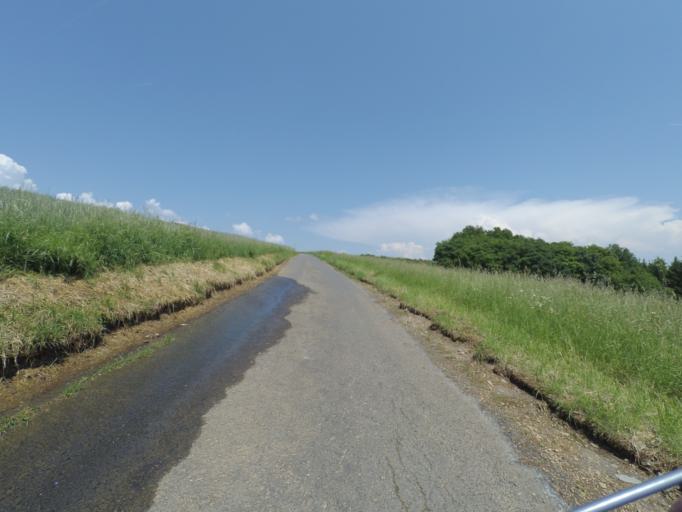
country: DE
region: Rheinland-Pfalz
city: Anschau
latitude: 50.2801
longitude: 7.1207
